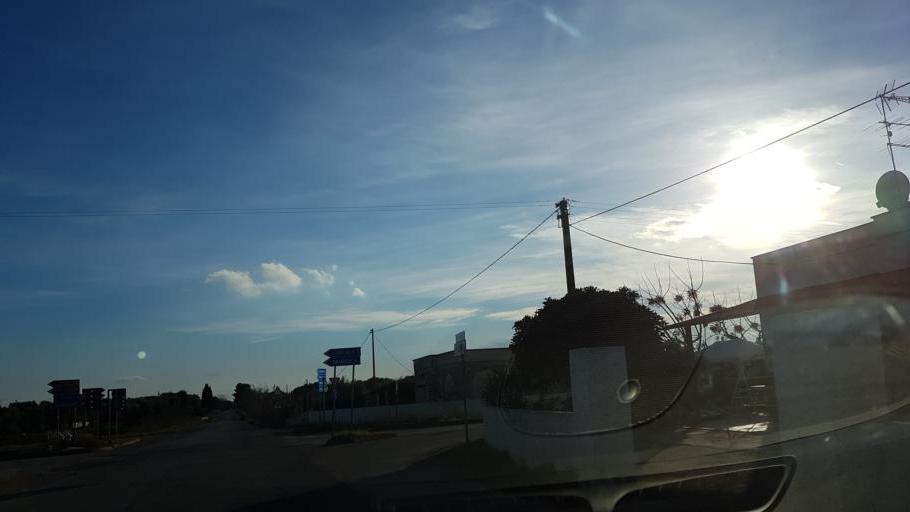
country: IT
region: Apulia
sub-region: Provincia di Brindisi
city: San Vito dei Normanni
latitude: 40.6651
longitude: 17.7793
